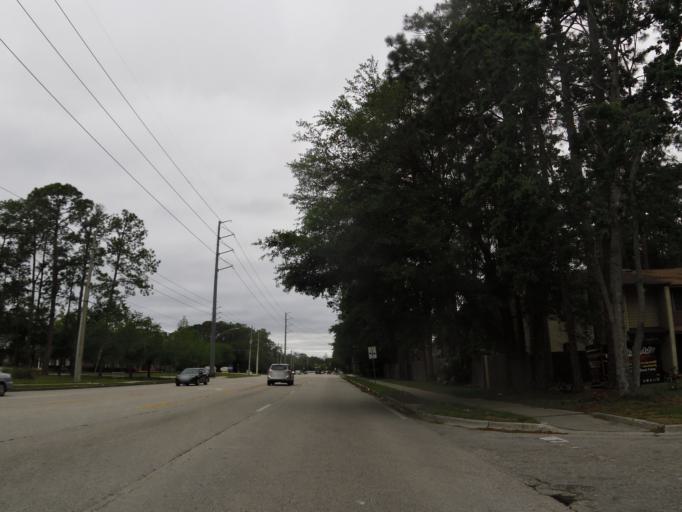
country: US
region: Florida
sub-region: Saint Johns County
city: Fruit Cove
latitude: 30.1804
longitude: -81.6062
